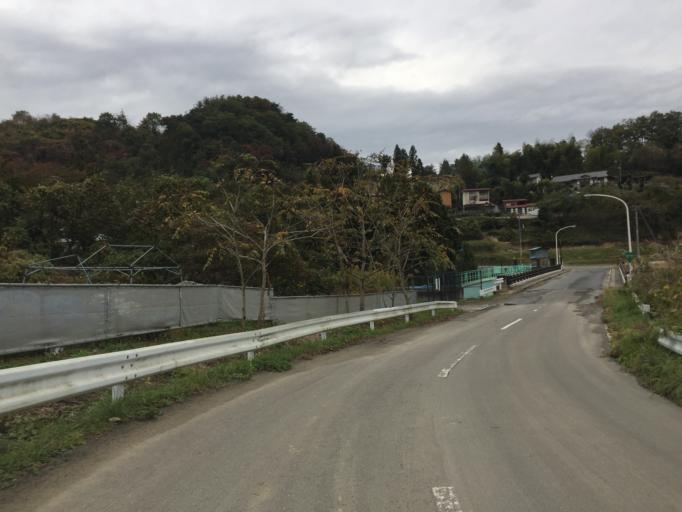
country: JP
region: Fukushima
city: Fukushima-shi
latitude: 37.8352
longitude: 140.4377
